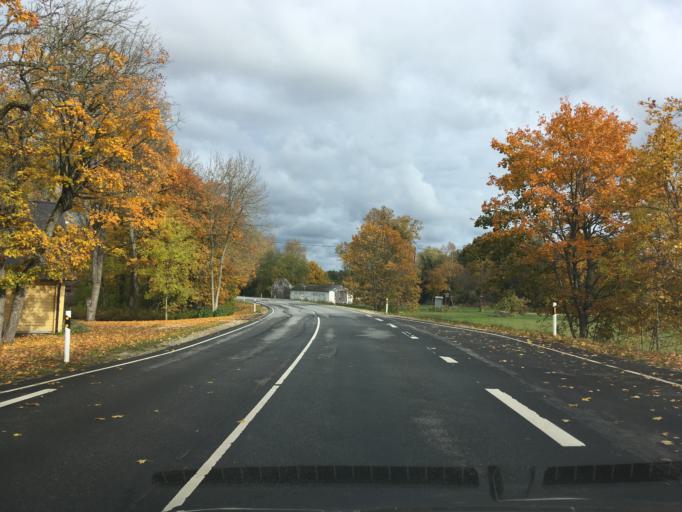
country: EE
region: Harju
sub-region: Anija vald
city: Kehra
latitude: 59.2813
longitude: 25.3733
